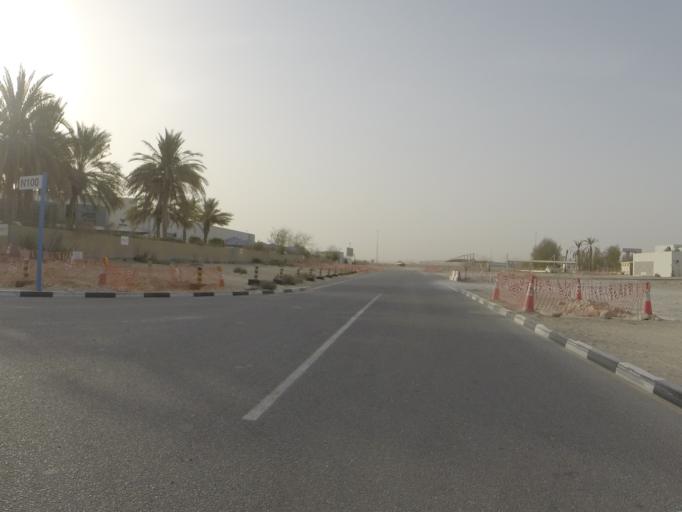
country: AE
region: Dubai
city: Dubai
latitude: 24.9522
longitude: 55.0671
